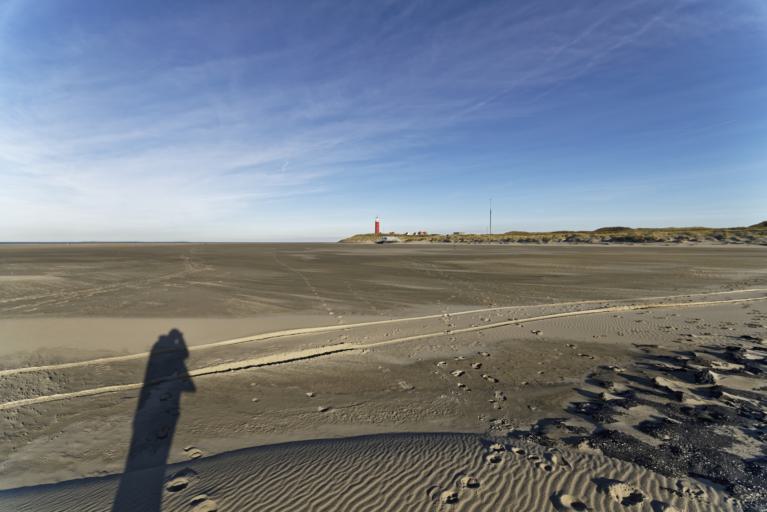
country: NL
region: North Holland
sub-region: Gemeente Texel
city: Den Burg
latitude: 53.1807
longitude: 4.8450
